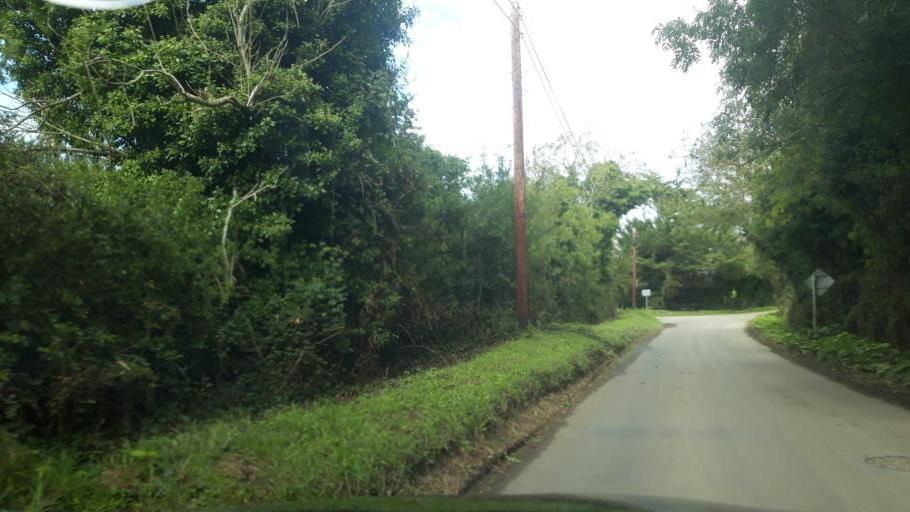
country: IE
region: Leinster
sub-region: Fingal County
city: Swords
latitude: 53.4910
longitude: -6.2848
